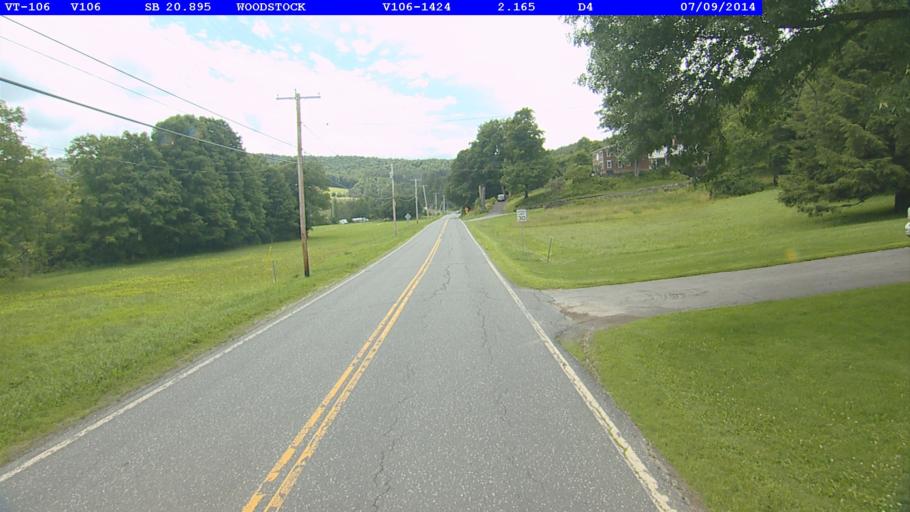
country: US
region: Vermont
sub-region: Windsor County
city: Woodstock
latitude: 43.5613
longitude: -72.5331
